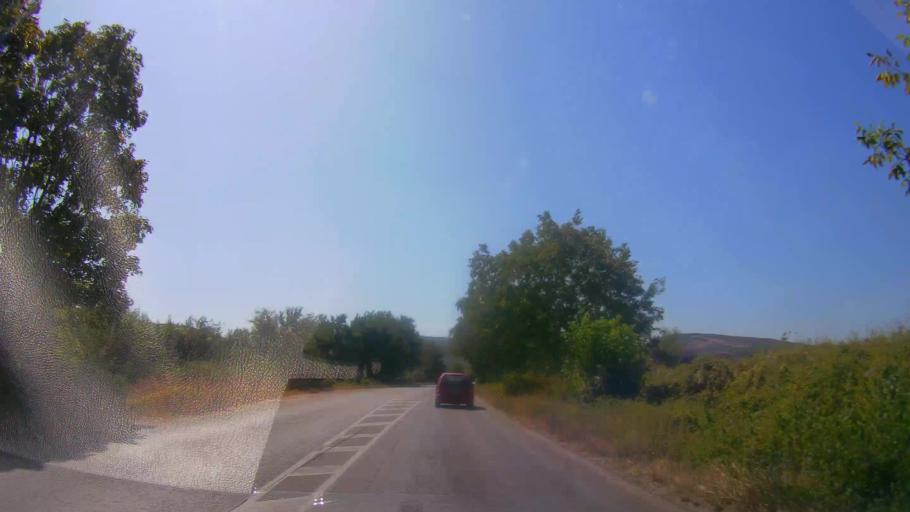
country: BG
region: Veliko Turnovo
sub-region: Obshtina Gorna Oryakhovitsa
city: Purvomaytsi
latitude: 43.1518
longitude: 25.6177
